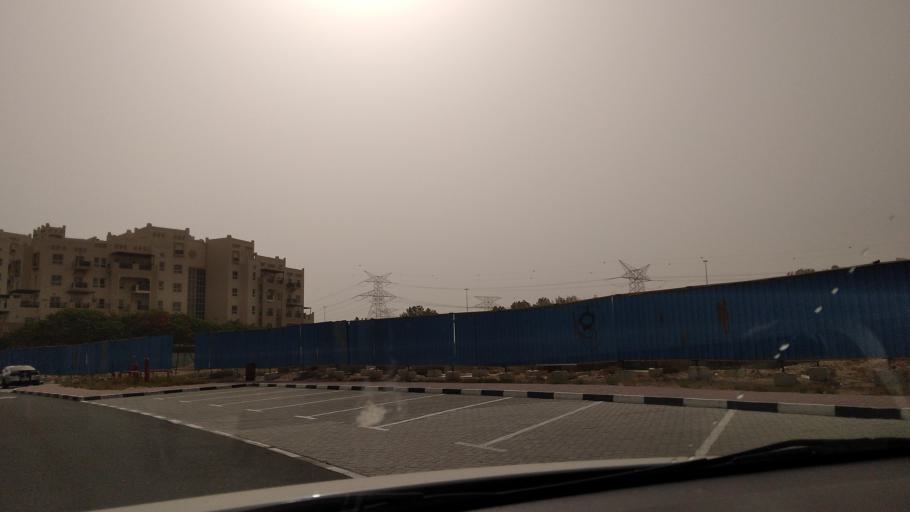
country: AE
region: Dubai
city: Dubai
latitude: 24.9993
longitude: 55.2542
